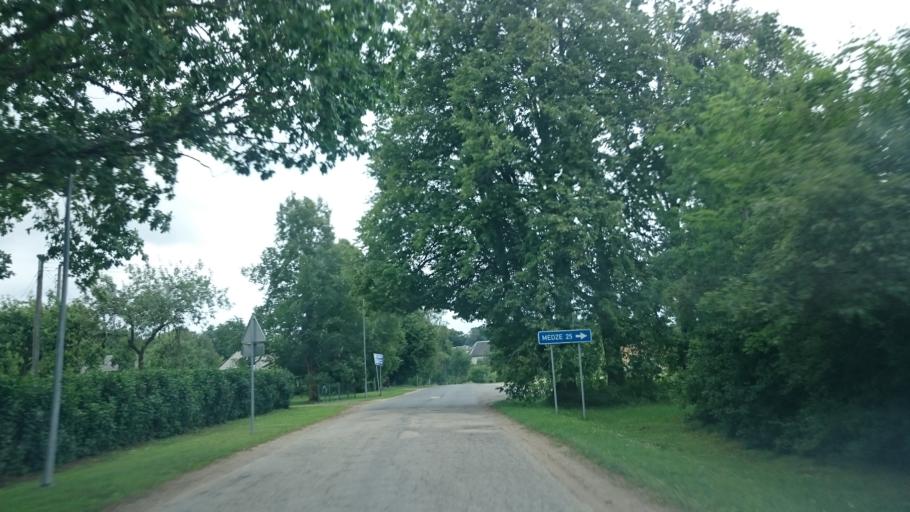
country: LV
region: Durbe
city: Liegi
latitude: 56.7389
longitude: 21.3815
